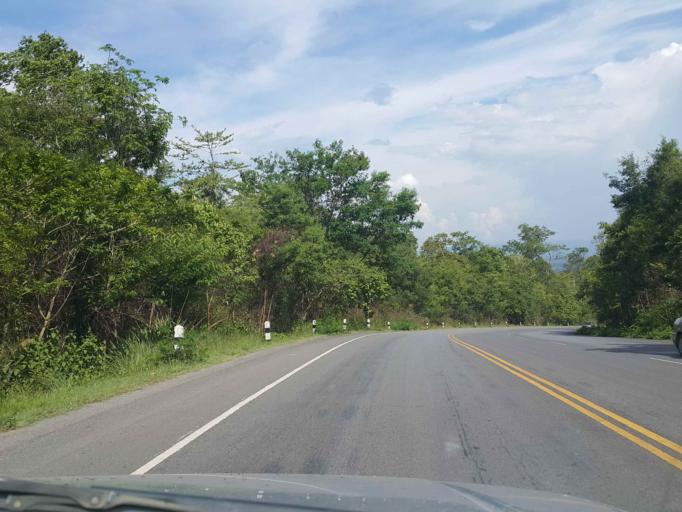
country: TH
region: Lampang
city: Wang Nuea
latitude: 19.1587
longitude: 99.5875
